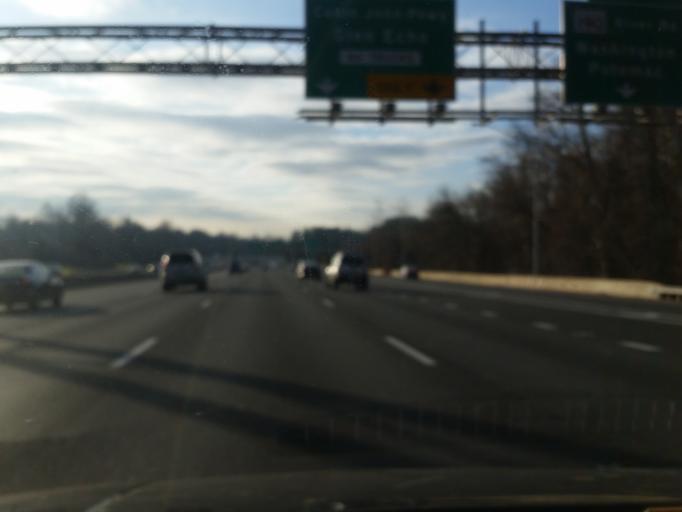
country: US
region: Maryland
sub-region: Montgomery County
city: Cabin John
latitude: 38.9943
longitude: -77.1581
